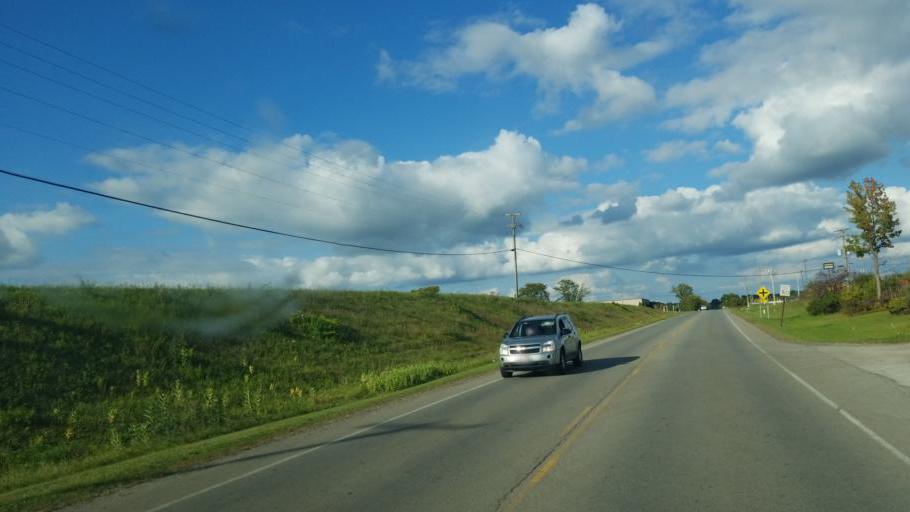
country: US
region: Ohio
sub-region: Richland County
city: Lincoln Heights
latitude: 40.7974
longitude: -82.5110
